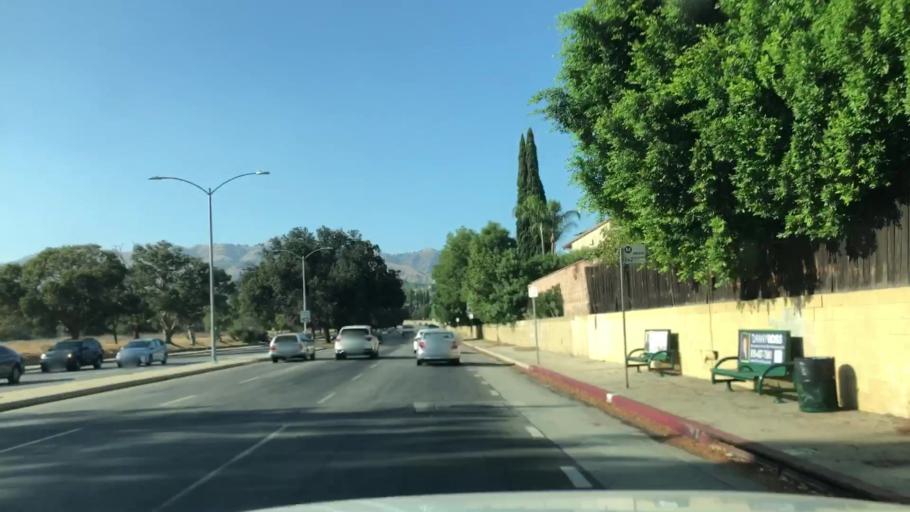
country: US
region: California
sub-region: Los Angeles County
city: Northridge
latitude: 34.2664
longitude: -118.5550
